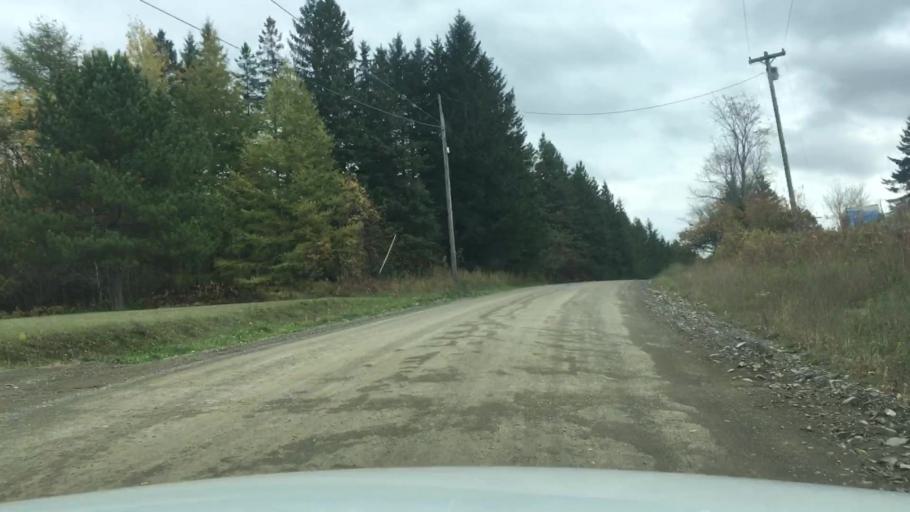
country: US
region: Maine
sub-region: Aroostook County
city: Easton
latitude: 46.5210
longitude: -67.8880
